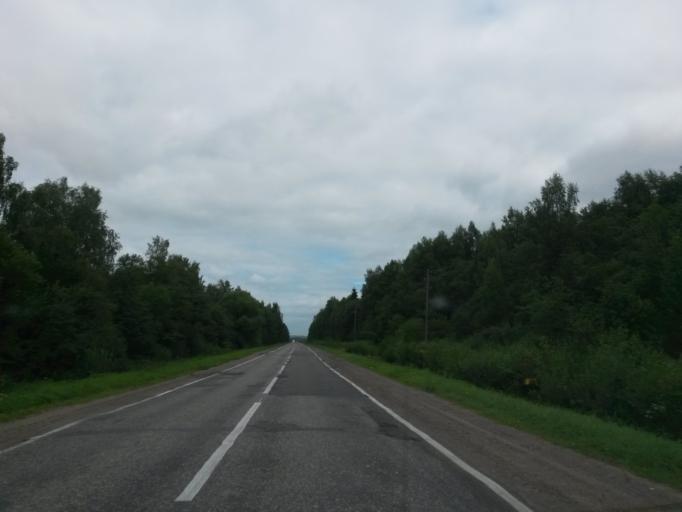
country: RU
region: Jaroslavl
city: Yaroslavl
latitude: 57.4970
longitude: 39.9002
